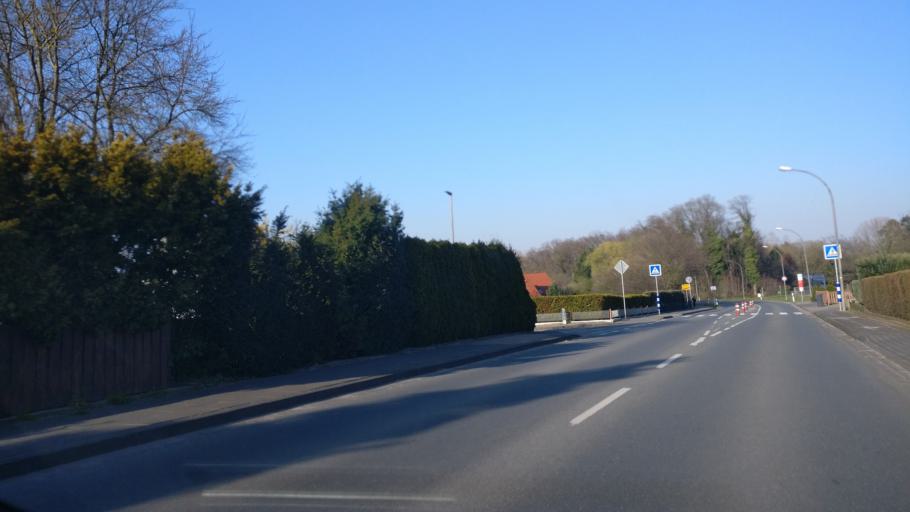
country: DE
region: North Rhine-Westphalia
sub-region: Regierungsbezirk Detmold
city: Leopoldshohe
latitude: 52.0123
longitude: 8.7467
